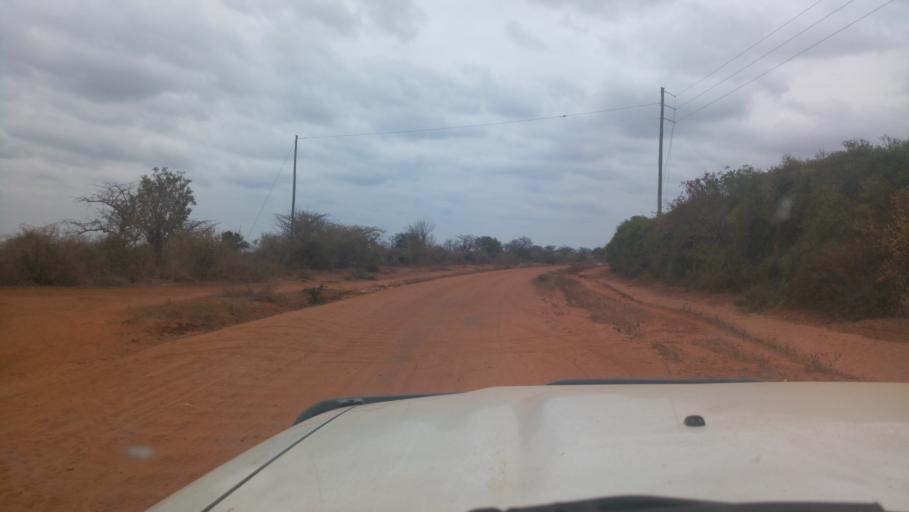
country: KE
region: Makueni
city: Wote
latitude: -1.9410
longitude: 38.0462
